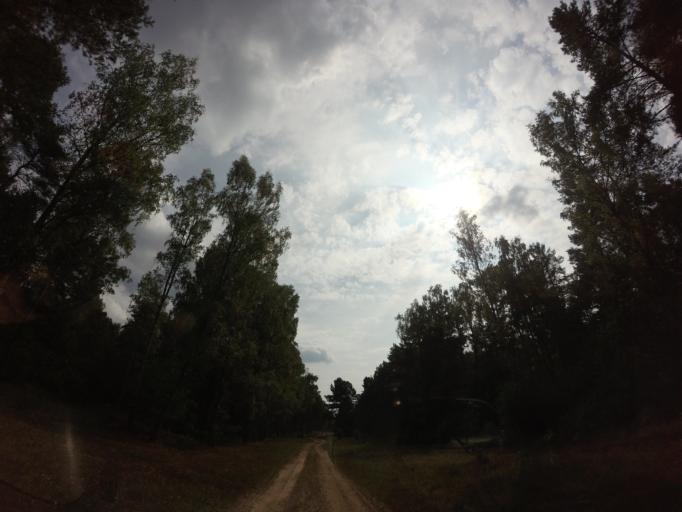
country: PL
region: West Pomeranian Voivodeship
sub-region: Powiat drawski
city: Drawsko Pomorskie
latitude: 53.4678
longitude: 15.7315
